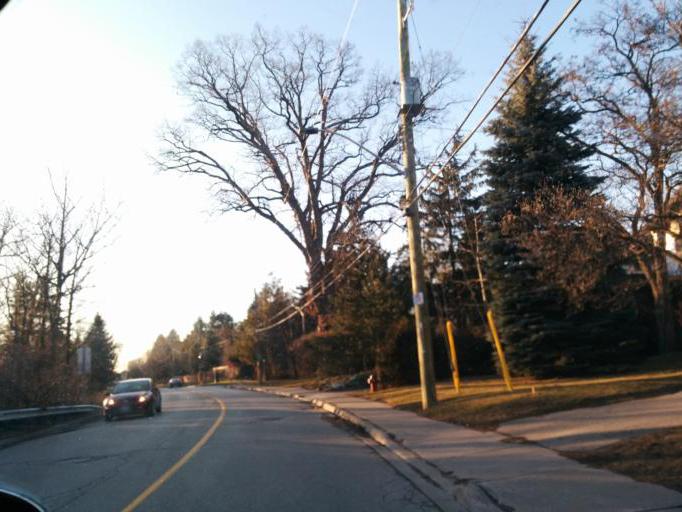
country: CA
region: Ontario
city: Mississauga
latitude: 43.5603
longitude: -79.6175
